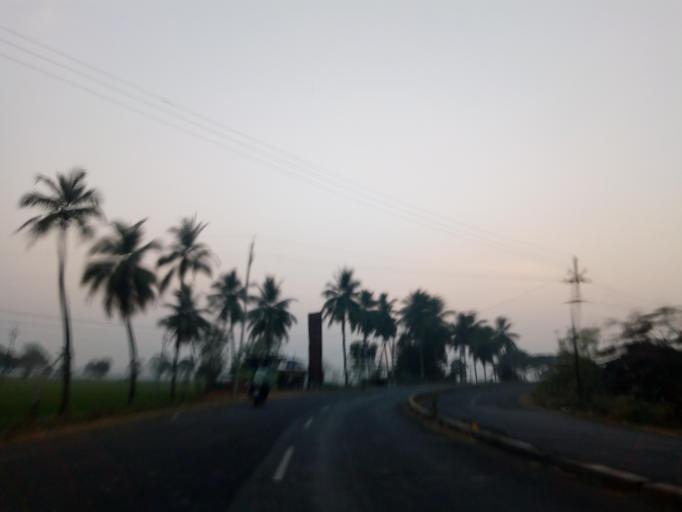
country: IN
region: Andhra Pradesh
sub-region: West Godavari
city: Tadepallegudem
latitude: 16.8208
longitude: 81.4759
